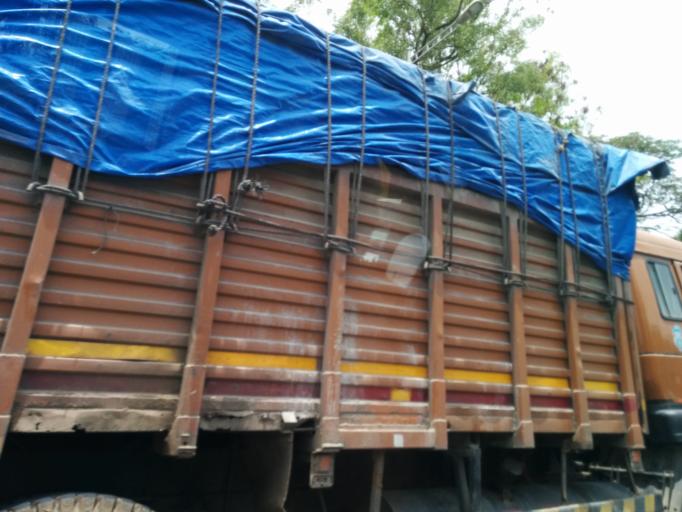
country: IN
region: Maharashtra
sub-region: Mumbai Suburban
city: Powai
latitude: 19.1342
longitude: 72.8745
